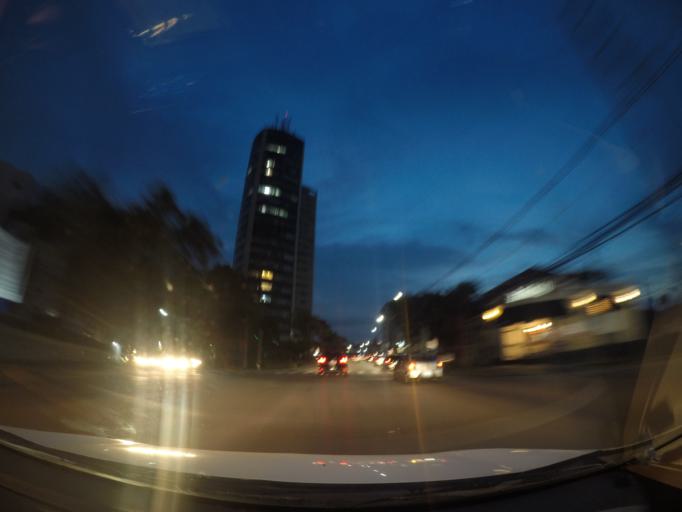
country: BR
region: Parana
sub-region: Curitiba
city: Curitiba
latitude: -25.4222
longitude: -49.2848
